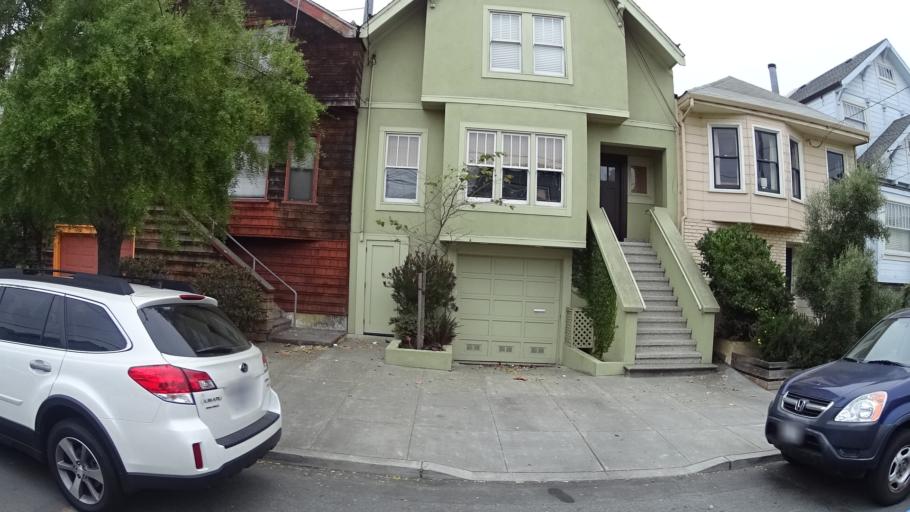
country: US
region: California
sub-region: San Francisco County
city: San Francisco
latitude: 37.7825
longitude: -122.4903
